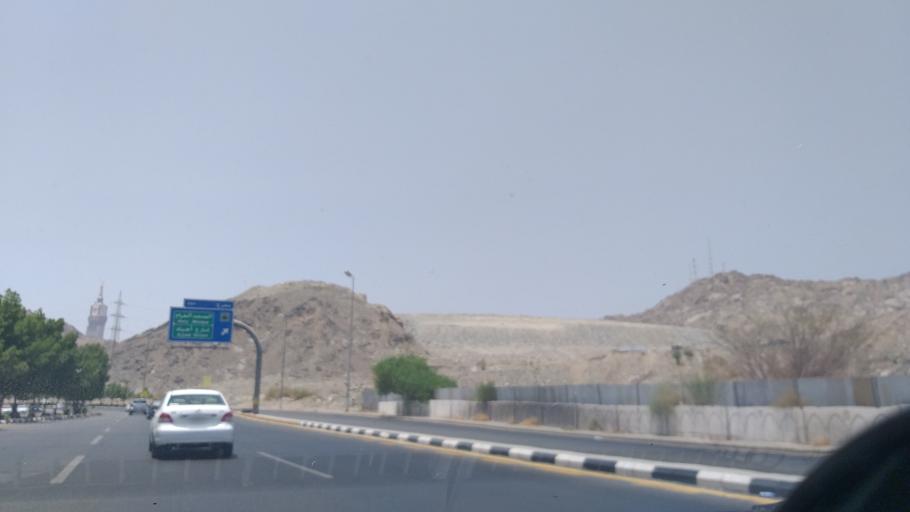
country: SA
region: Makkah
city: Mecca
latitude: 21.3932
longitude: 39.8550
